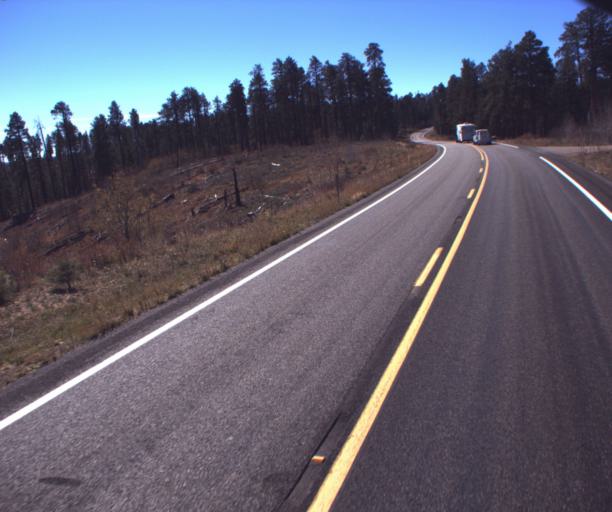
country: US
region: Arizona
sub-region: Coconino County
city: Fredonia
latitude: 36.6323
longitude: -112.1733
